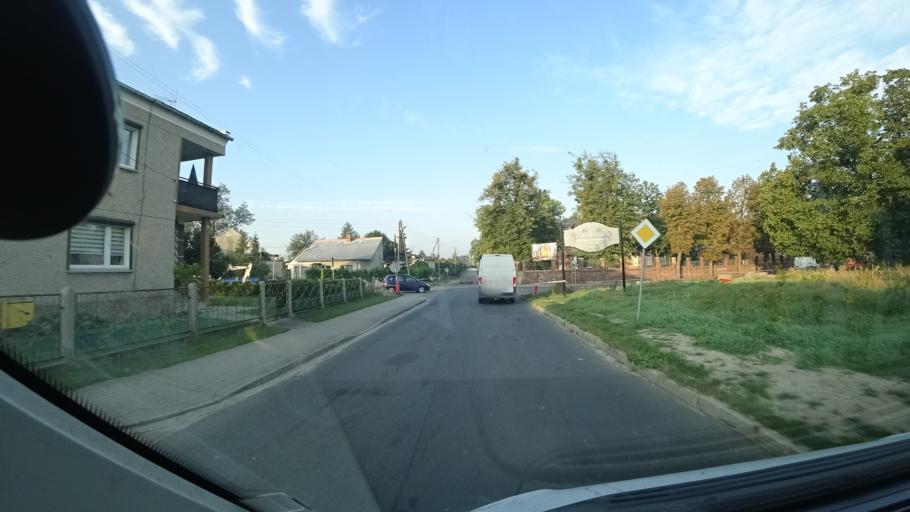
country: PL
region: Opole Voivodeship
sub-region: Powiat kedzierzynsko-kozielski
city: Slawiecice
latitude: 50.3748
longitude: 18.3295
